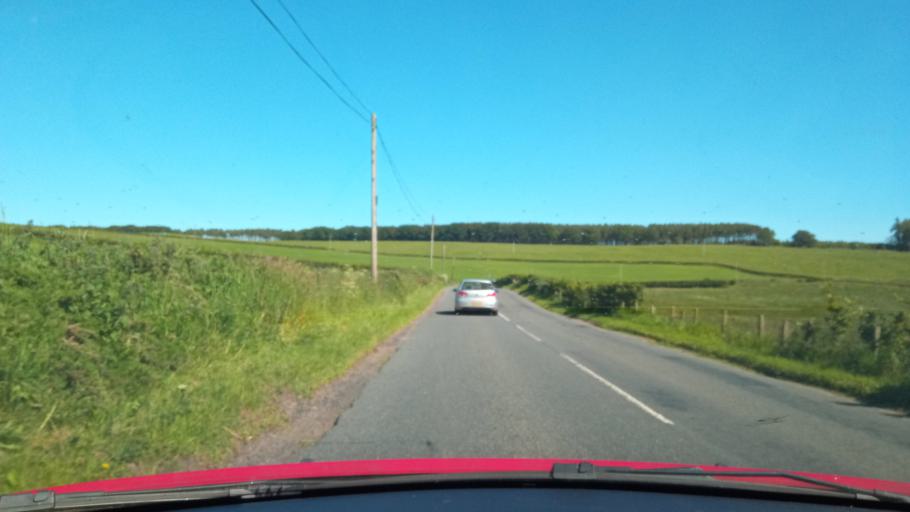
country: GB
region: Scotland
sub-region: The Scottish Borders
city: Duns
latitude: 55.8326
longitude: -2.3310
